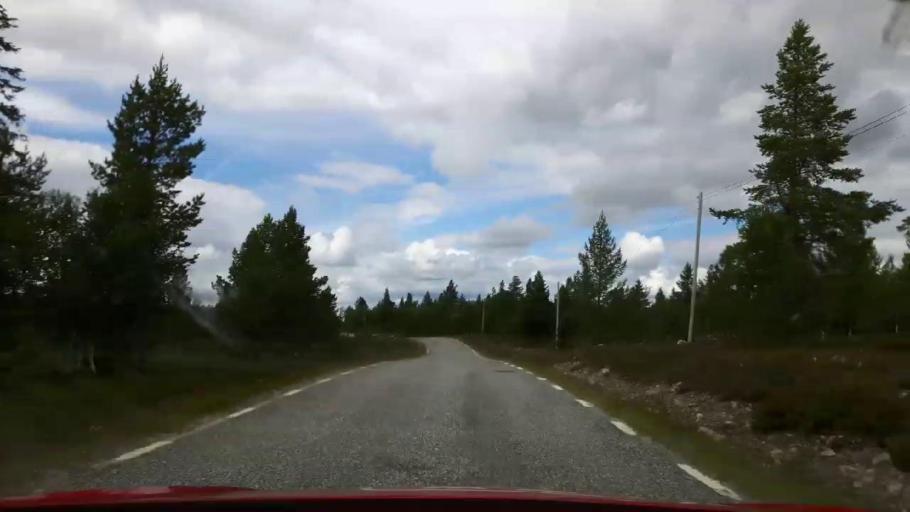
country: NO
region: Hedmark
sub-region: Engerdal
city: Engerdal
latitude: 62.3337
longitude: 12.8046
